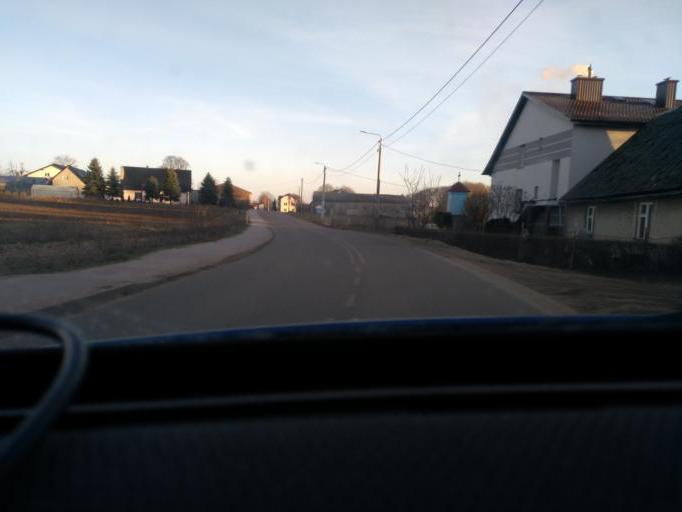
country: PL
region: Pomeranian Voivodeship
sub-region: Powiat kartuski
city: Przodkowo
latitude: 54.4126
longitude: 18.3210
